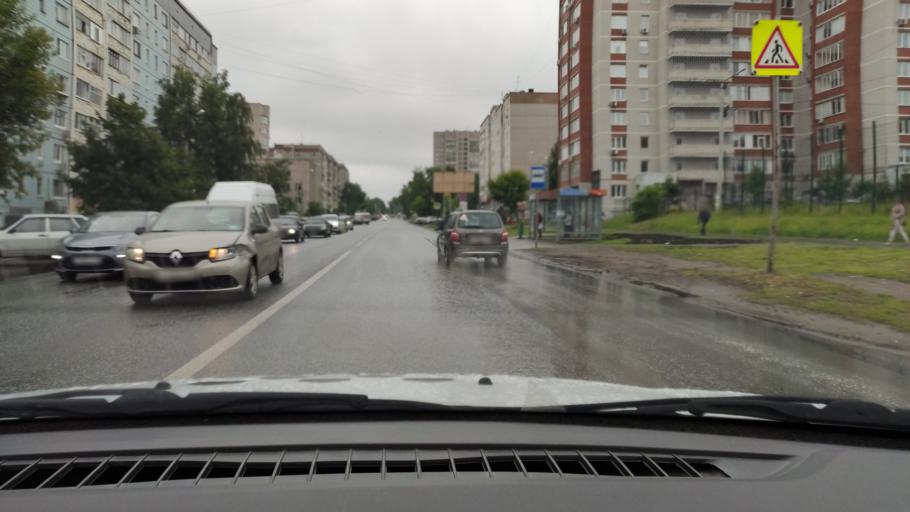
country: RU
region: Udmurtiya
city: Izhevsk
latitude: 56.8757
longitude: 53.2140
